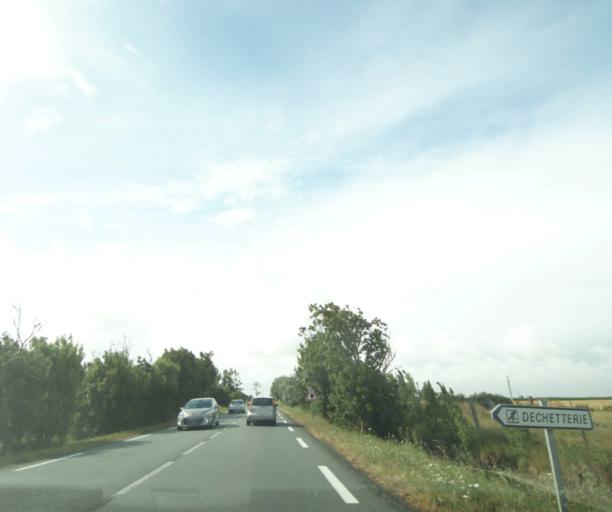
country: FR
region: Poitou-Charentes
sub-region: Departement de la Charente-Maritime
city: Charron
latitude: 46.2922
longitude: -1.0846
